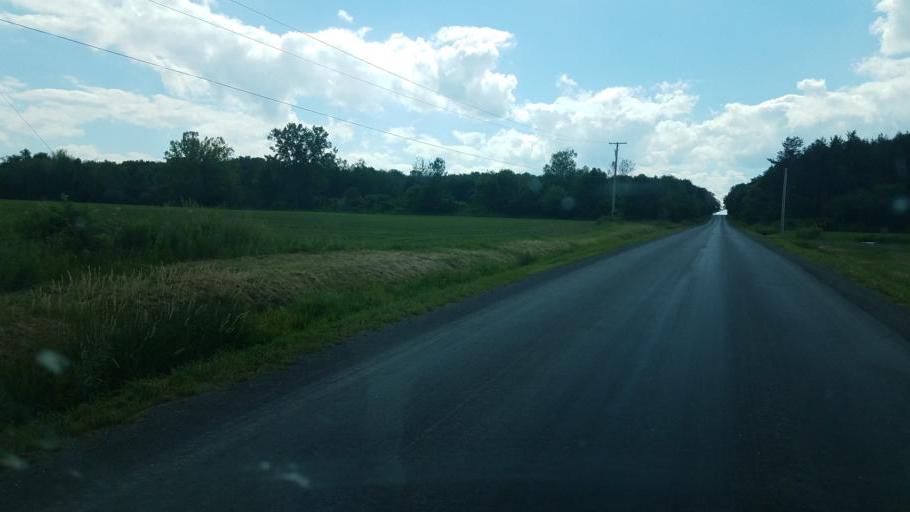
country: US
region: New York
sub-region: Yates County
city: Dundee
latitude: 42.5596
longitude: -77.0366
